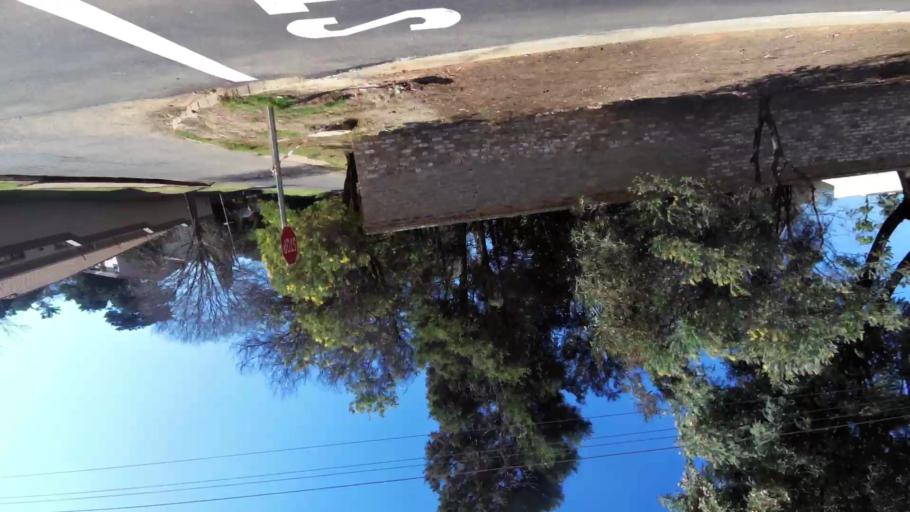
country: ZA
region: Gauteng
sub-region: City of Johannesburg Metropolitan Municipality
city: Roodepoort
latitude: -26.1460
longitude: 27.9437
